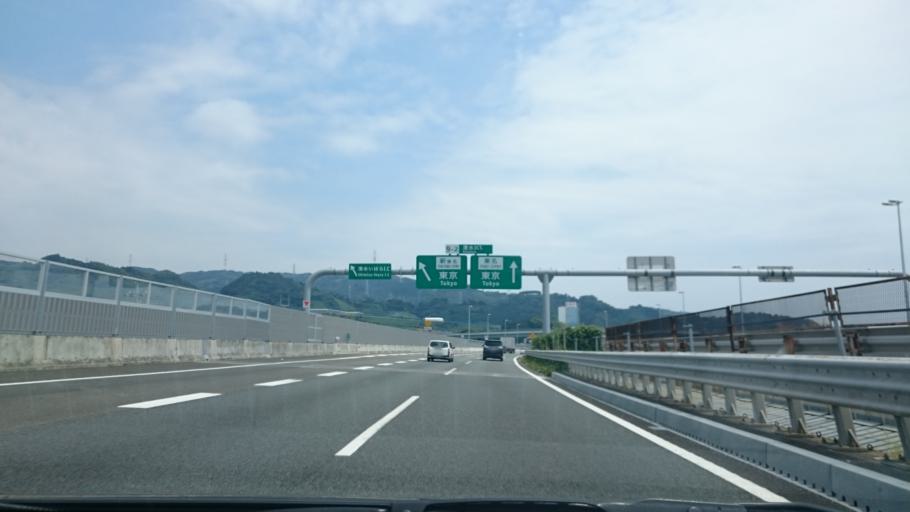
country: JP
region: Shizuoka
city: Shizuoka-shi
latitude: 35.0453
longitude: 138.4822
